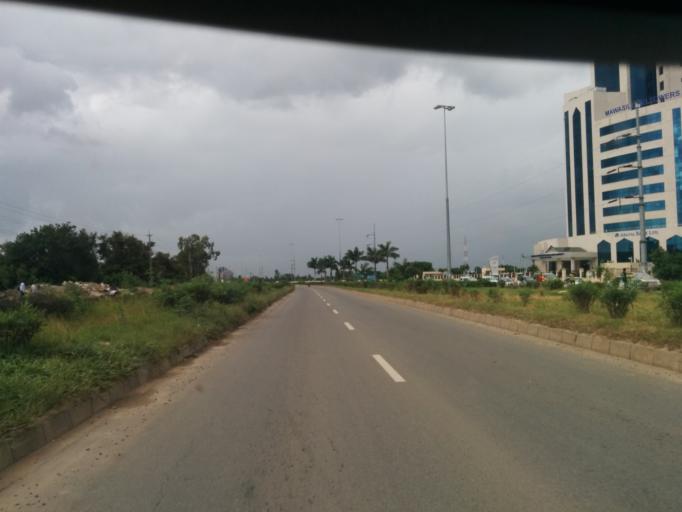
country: TZ
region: Dar es Salaam
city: Magomeni
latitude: -6.7847
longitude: 39.2124
